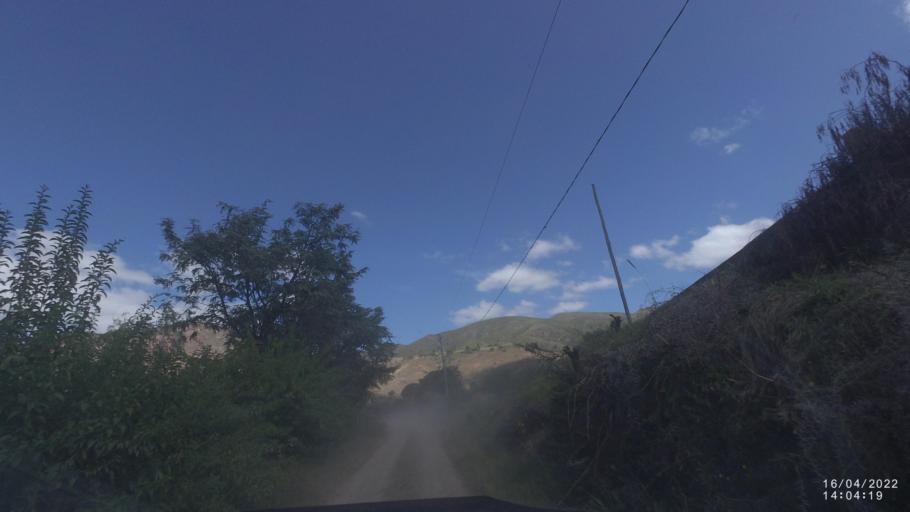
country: BO
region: Cochabamba
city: Mizque
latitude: -18.0551
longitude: -65.5409
